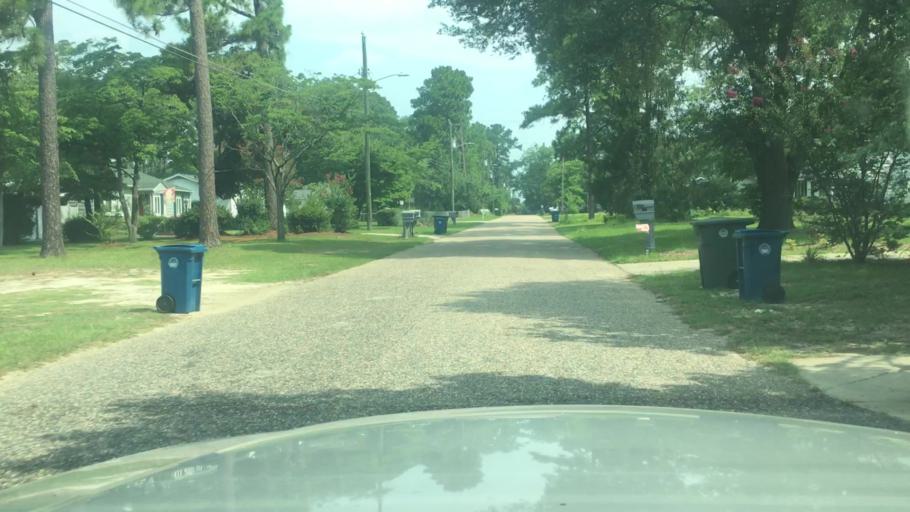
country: US
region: North Carolina
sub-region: Cumberland County
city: Hope Mills
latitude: 35.0352
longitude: -78.9432
